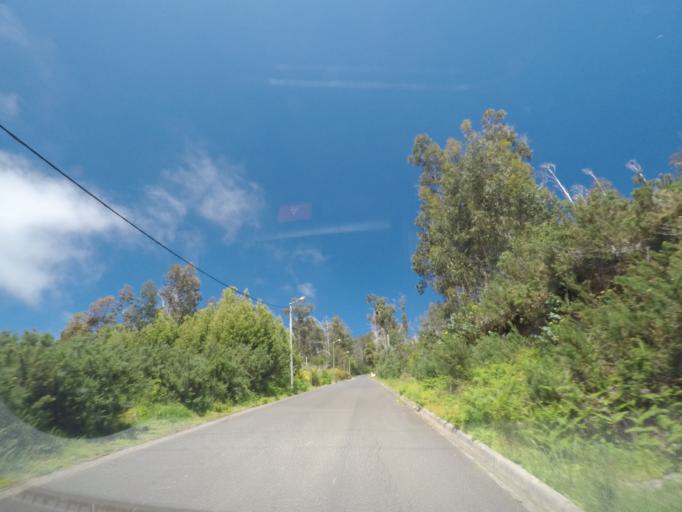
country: PT
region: Madeira
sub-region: Calheta
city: Arco da Calheta
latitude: 32.7290
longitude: -17.1341
